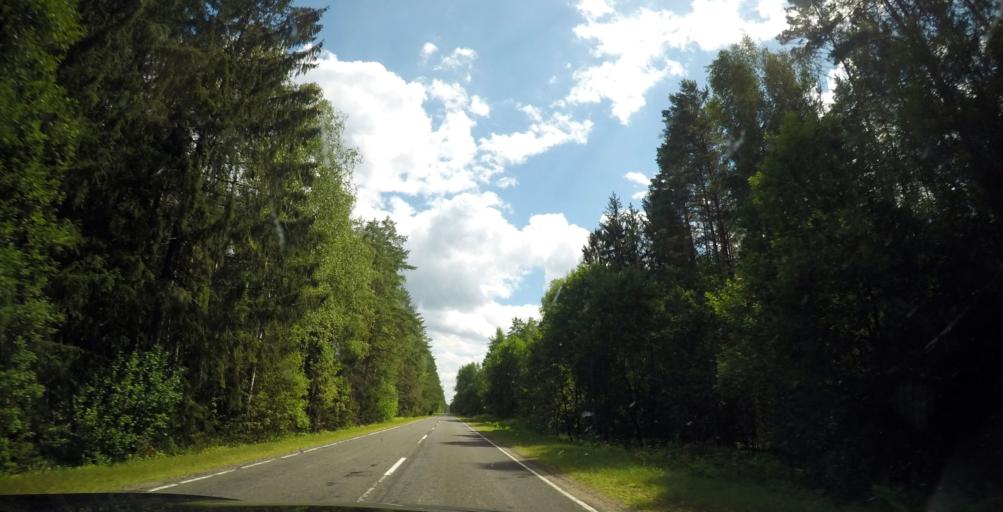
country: BY
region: Grodnenskaya
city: Skidal'
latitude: 53.8468
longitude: 24.2032
